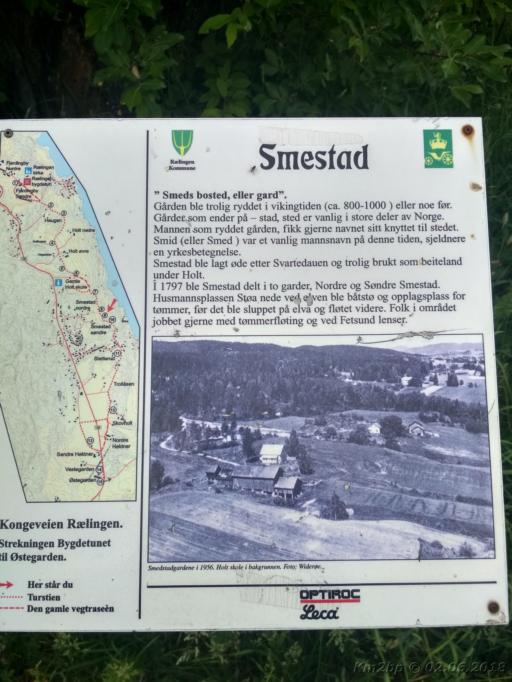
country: NO
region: Akershus
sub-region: Raelingen
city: Fjerdingby
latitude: 59.9054
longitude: 11.1004
